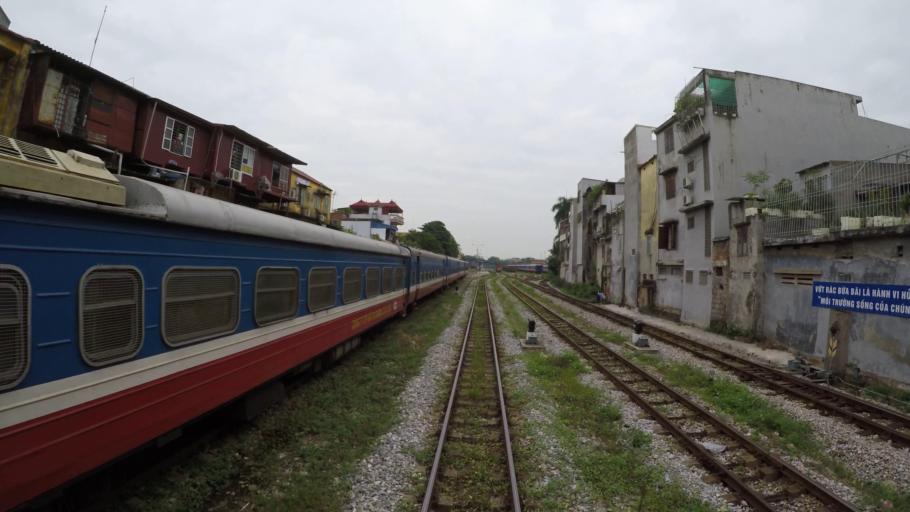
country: VN
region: Hai Phong
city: Haiphong
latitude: 20.8515
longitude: 106.6747
